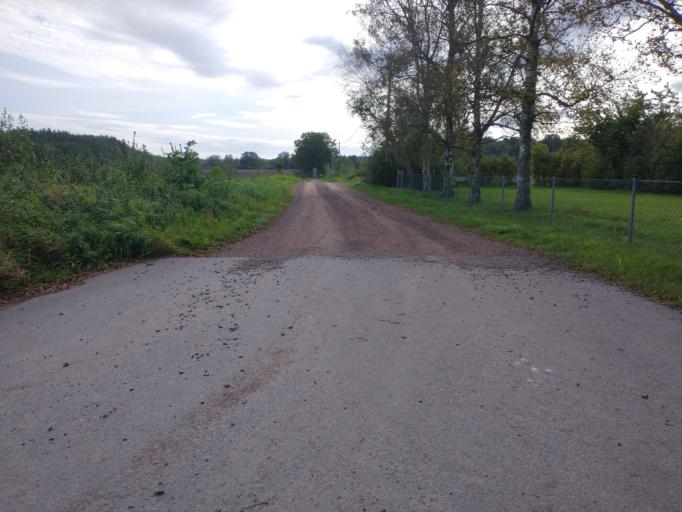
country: SE
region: Kalmar
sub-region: Kalmar Kommun
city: Lindsdal
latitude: 56.7778
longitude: 16.3088
